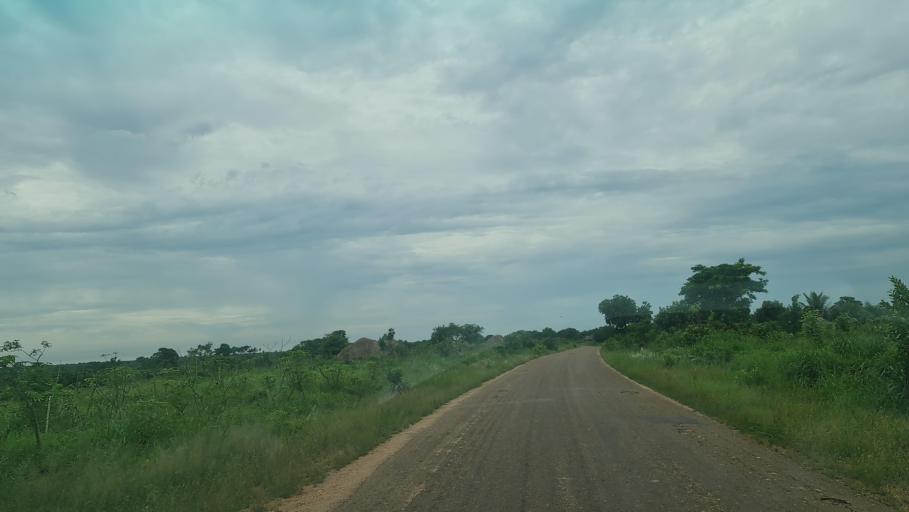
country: MW
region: Southern Region
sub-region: Nsanje District
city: Nsanje
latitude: -17.6866
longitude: 35.7294
